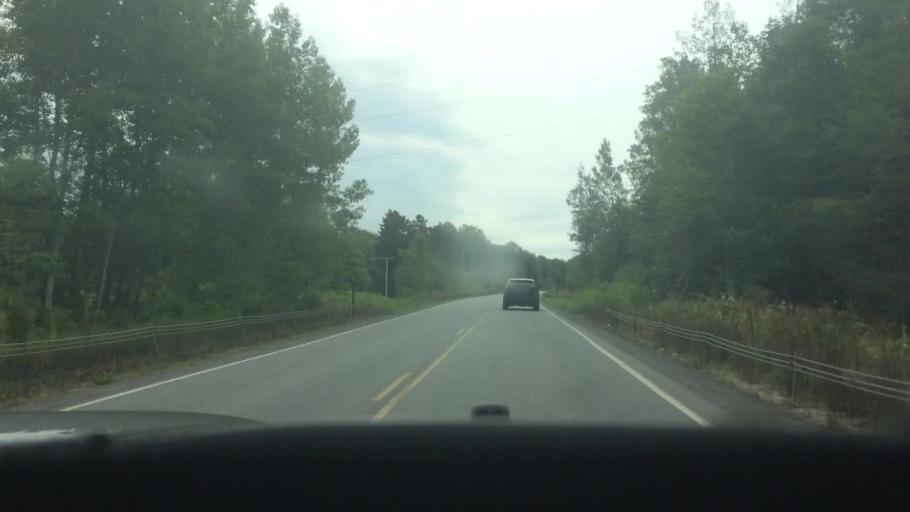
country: US
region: New York
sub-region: St. Lawrence County
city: Canton
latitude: 44.4817
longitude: -75.2450
